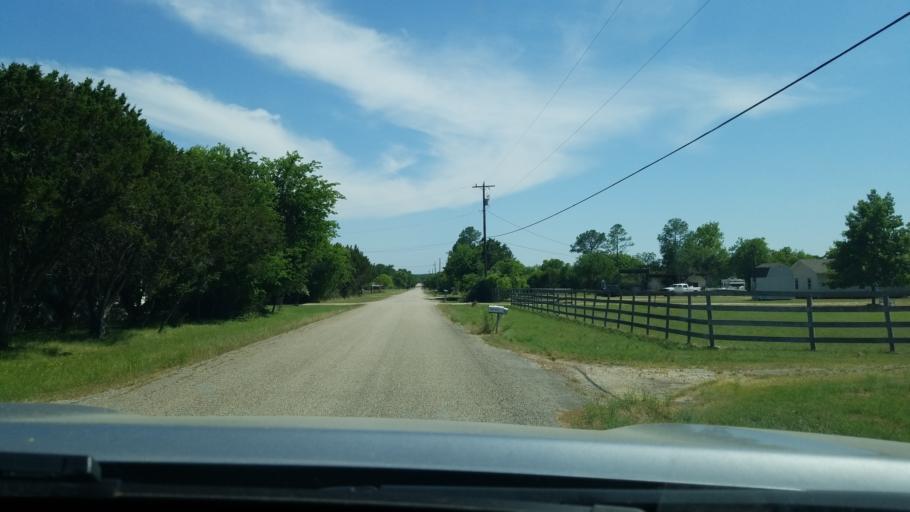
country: US
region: Texas
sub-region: Bexar County
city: Timberwood Park
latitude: 29.7560
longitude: -98.5179
